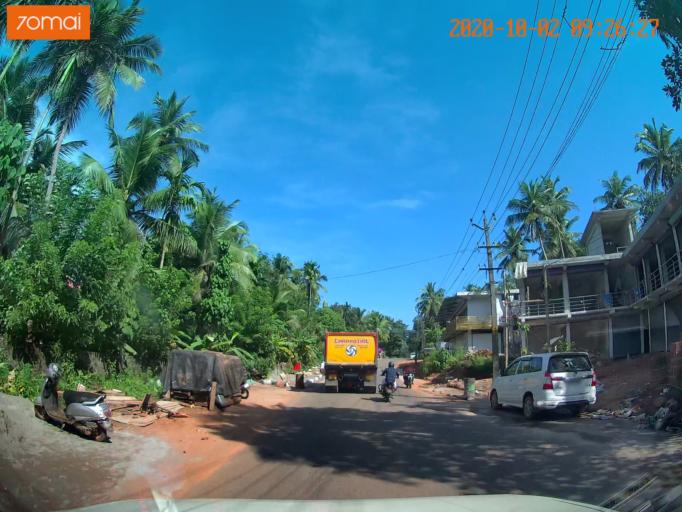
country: IN
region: Kerala
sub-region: Kozhikode
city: Naduvannur
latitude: 11.5925
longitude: 75.7666
